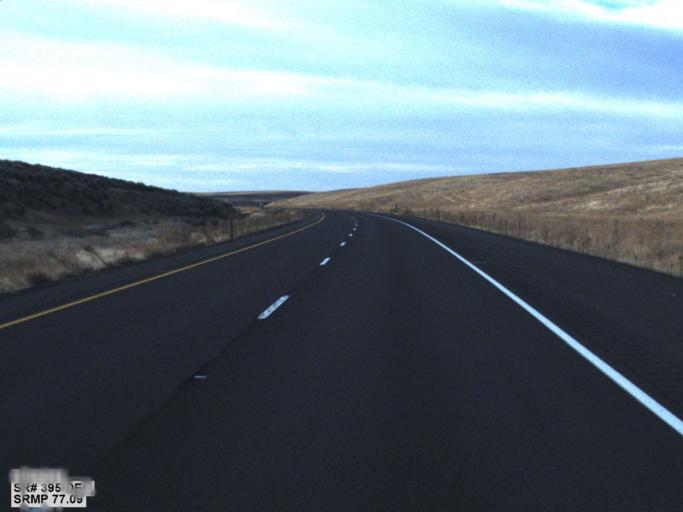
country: US
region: Washington
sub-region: Adams County
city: Ritzville
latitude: 46.9040
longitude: -118.6134
